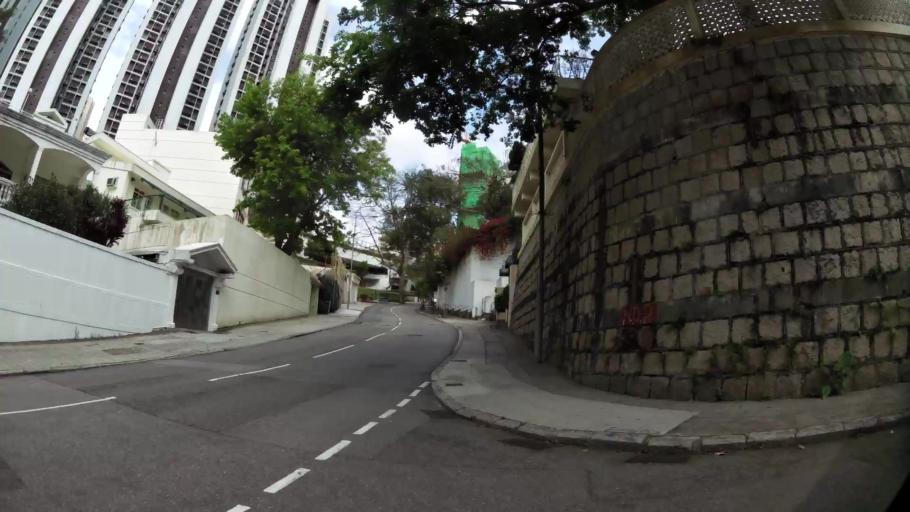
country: HK
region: Wanchai
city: Wan Chai
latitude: 22.2697
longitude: 114.1919
